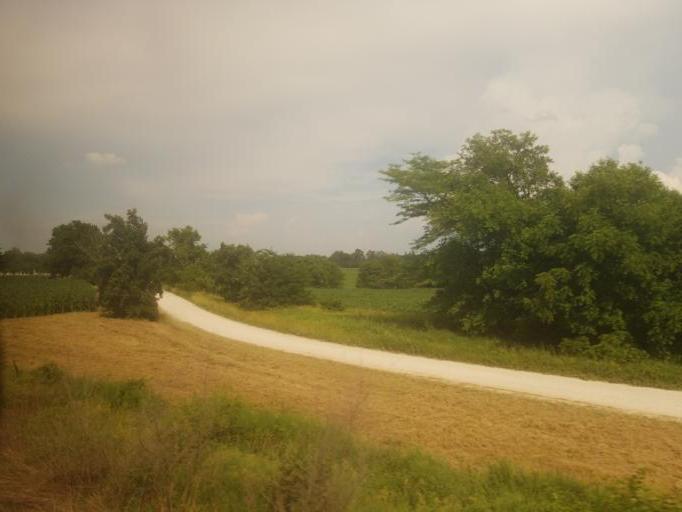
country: US
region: Illinois
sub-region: Henry County
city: Galva
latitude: 41.1084
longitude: -90.1698
